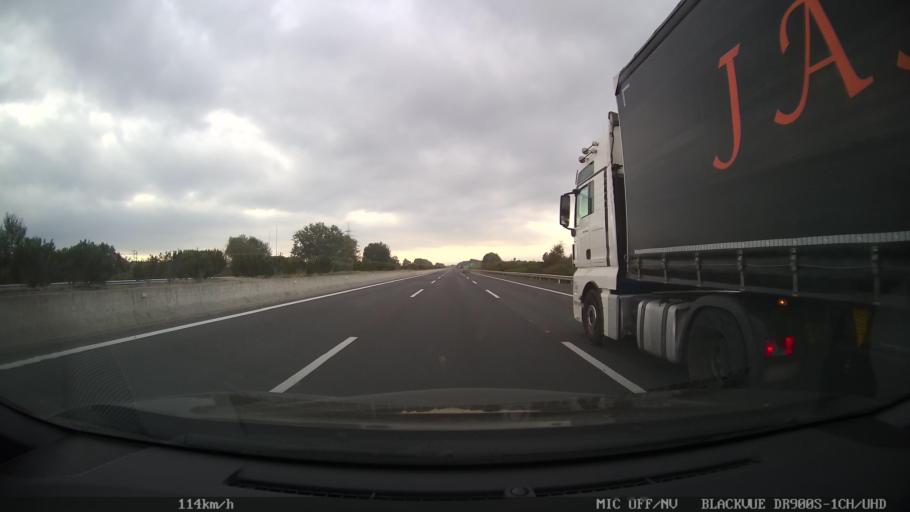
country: GR
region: Central Macedonia
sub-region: Nomos Pierias
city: Nea Efesos
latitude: 40.2184
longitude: 22.5420
